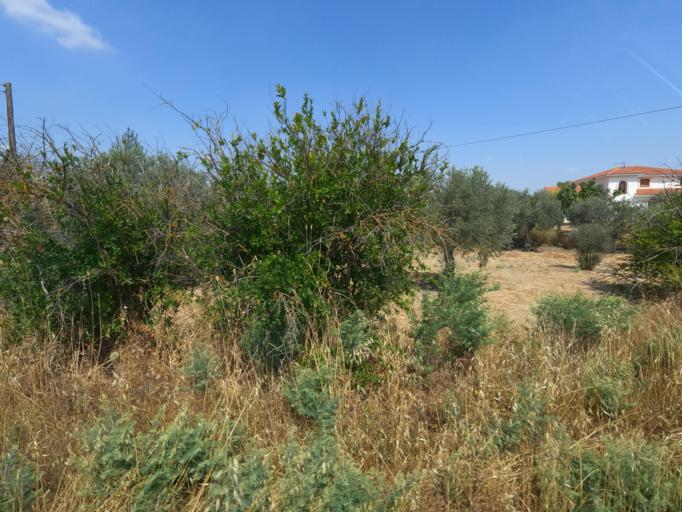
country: CY
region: Lefkosia
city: Dali
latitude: 35.0352
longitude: 33.4344
